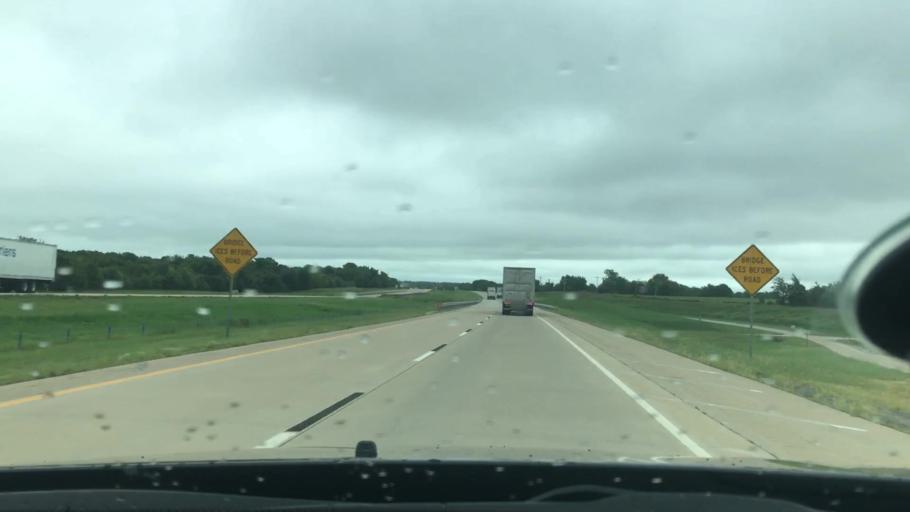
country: US
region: Oklahoma
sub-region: McIntosh County
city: Checotah
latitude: 35.4545
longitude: -95.6485
